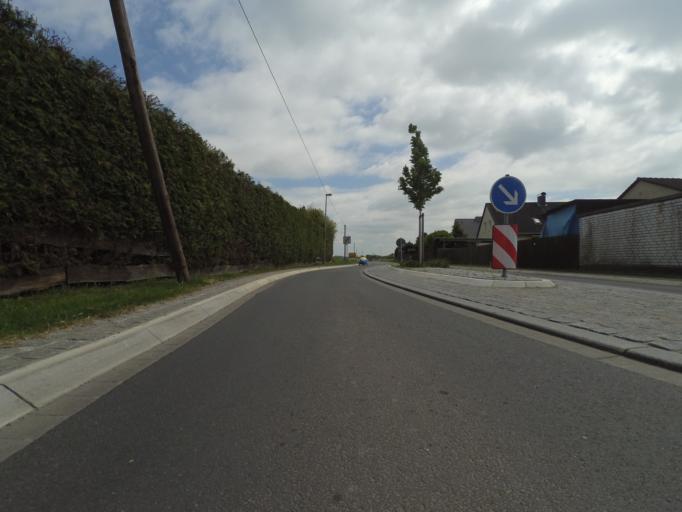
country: DE
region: Lower Saxony
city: Lehrte
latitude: 52.4081
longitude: 9.9930
